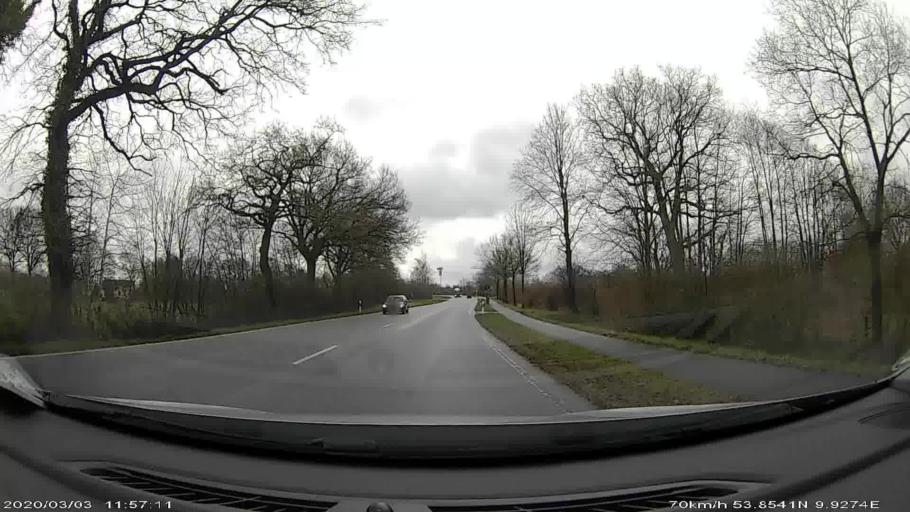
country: DE
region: Schleswig-Holstein
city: Nutzen
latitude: 53.8523
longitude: 9.9292
